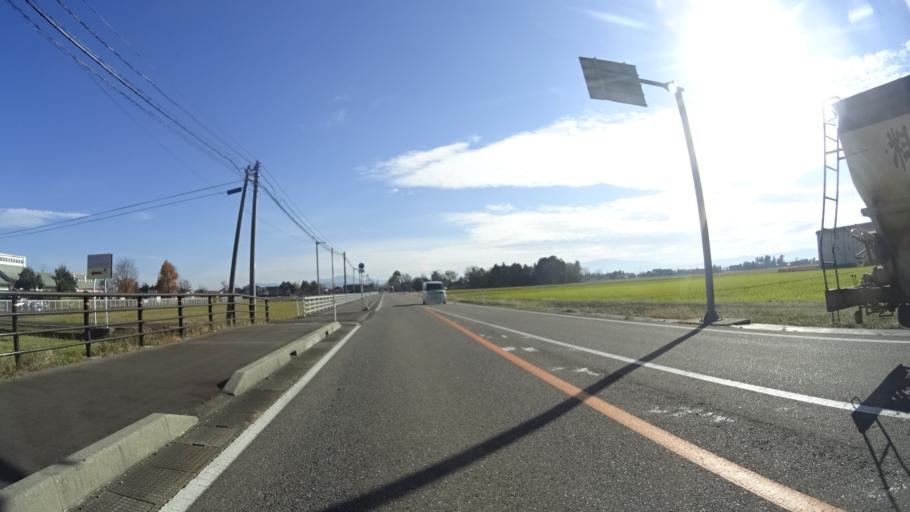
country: JP
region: Niigata
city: Mitsuke
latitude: 37.5550
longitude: 138.8505
